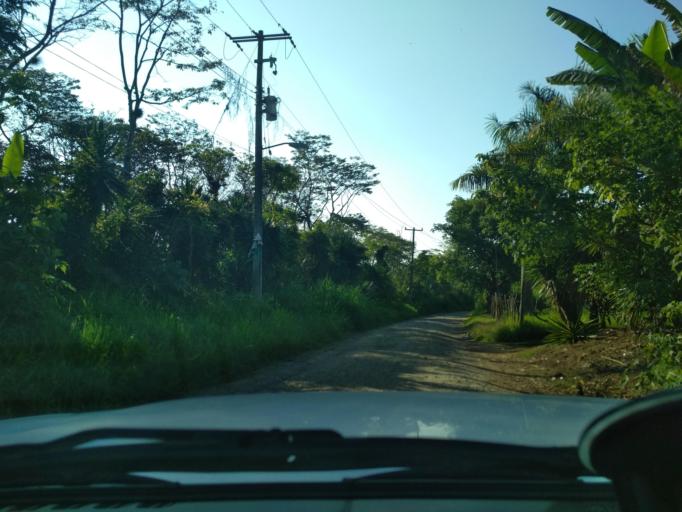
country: MX
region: Veracruz
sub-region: Fortin
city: Fraccionamiento Villas de la Llave
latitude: 18.9221
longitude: -96.9914
